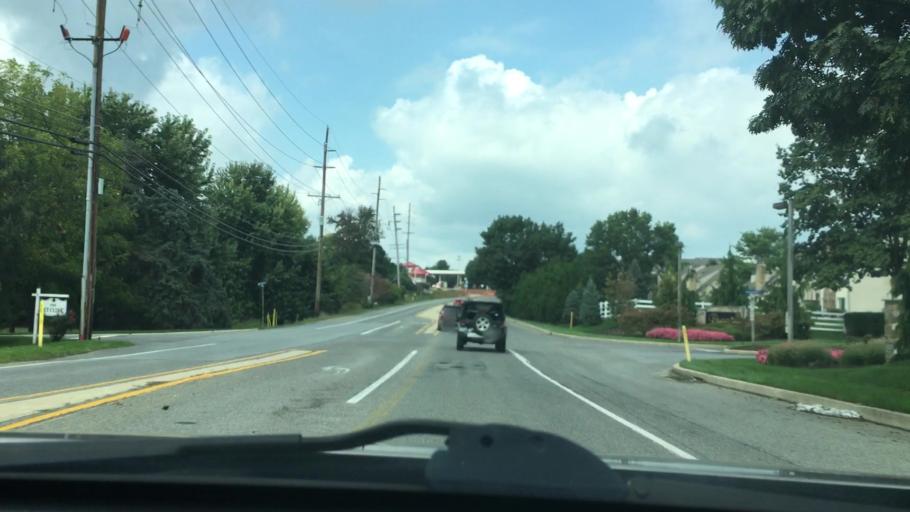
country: US
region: Pennsylvania
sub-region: Chester County
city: Malvern
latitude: 39.9632
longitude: -75.5201
